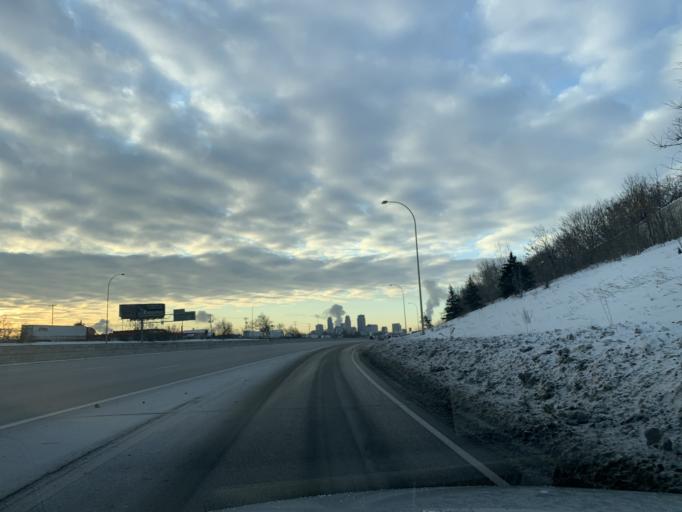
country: US
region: Minnesota
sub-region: Anoka County
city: Columbia Heights
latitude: 45.0201
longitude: -93.2831
